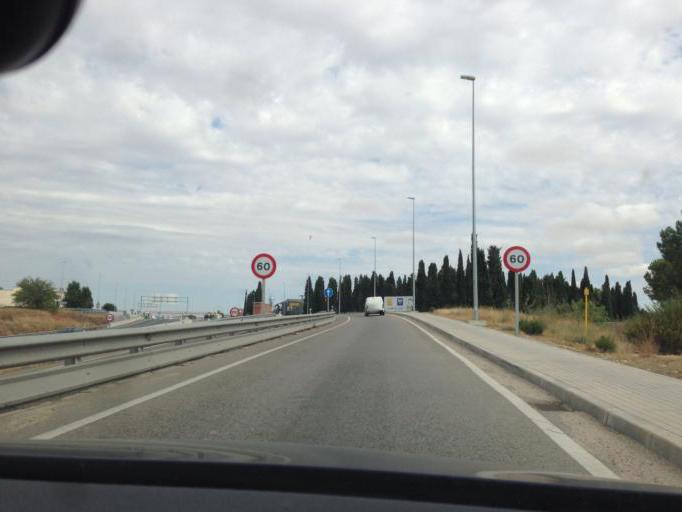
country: ES
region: Madrid
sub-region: Provincia de Madrid
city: Alcala de Henares
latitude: 40.5015
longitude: -3.3973
